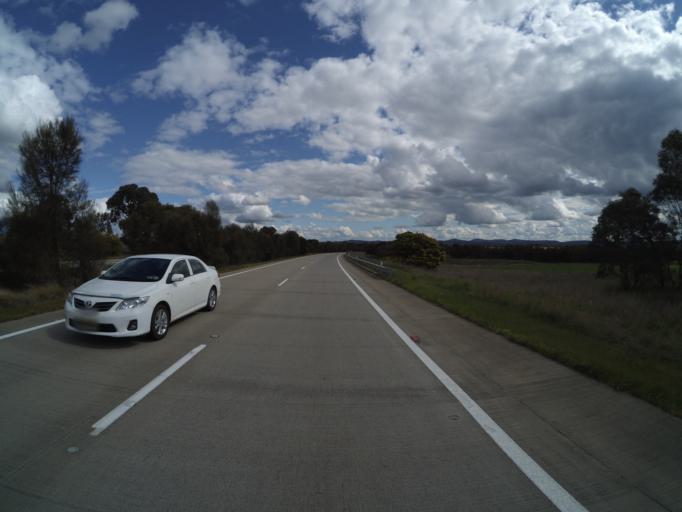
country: AU
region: New South Wales
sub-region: Yass Valley
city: Murrumbateman
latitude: -34.7975
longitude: 149.1604
